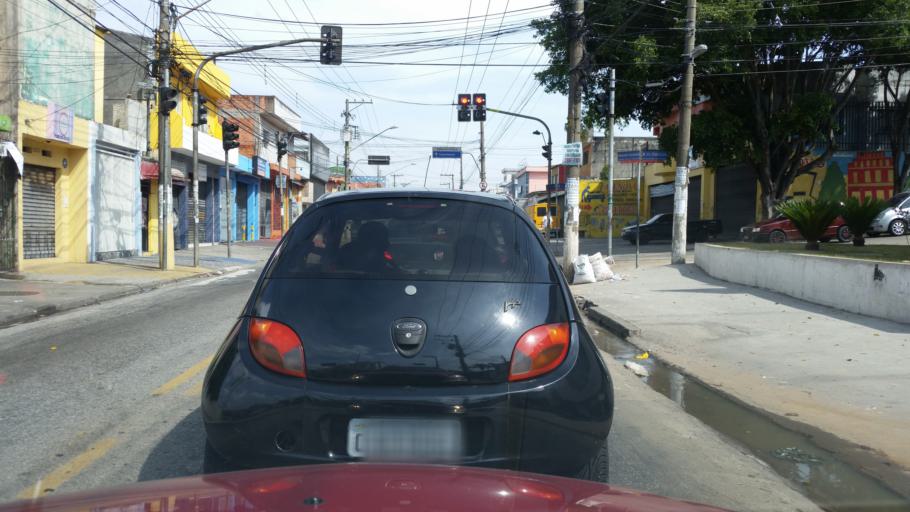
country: BR
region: Sao Paulo
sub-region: Ferraz De Vasconcelos
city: Ferraz de Vasconcelos
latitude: -23.5388
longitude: -46.4267
